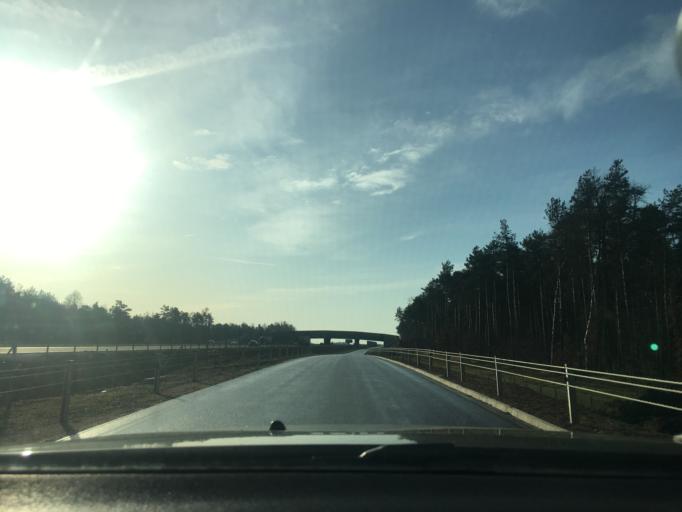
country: PL
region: Swietokrzyskie
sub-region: Powiat jedrzejowski
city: Jedrzejow
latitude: 50.6756
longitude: 20.3477
